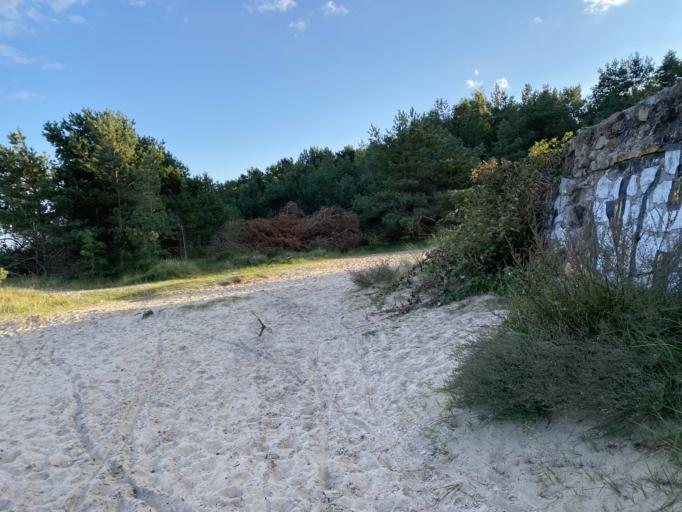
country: DE
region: Mecklenburg-Vorpommern
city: Ostseebad Binz
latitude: 54.4476
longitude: 13.5733
